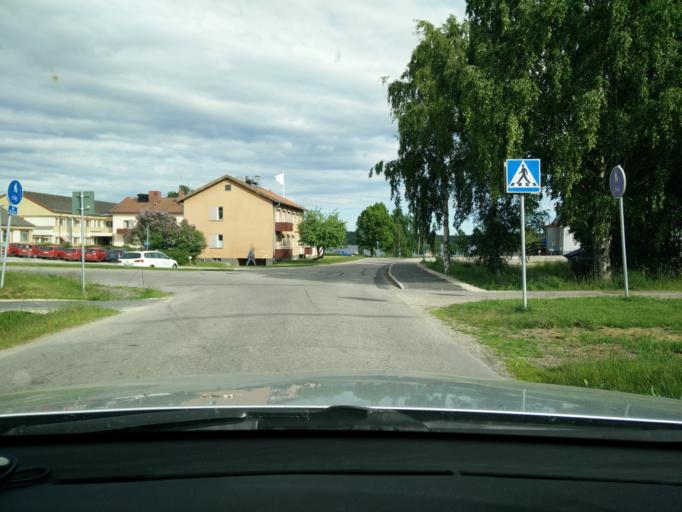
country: SE
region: Gaevleborg
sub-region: Nordanstigs Kommun
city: Bergsjoe
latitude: 61.9809
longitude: 17.0579
